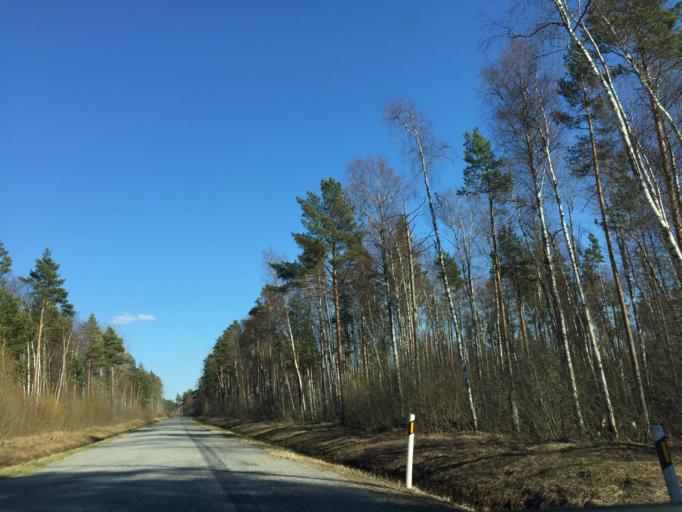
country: RU
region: Pskov
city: Gdov
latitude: 59.0101
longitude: 27.6384
